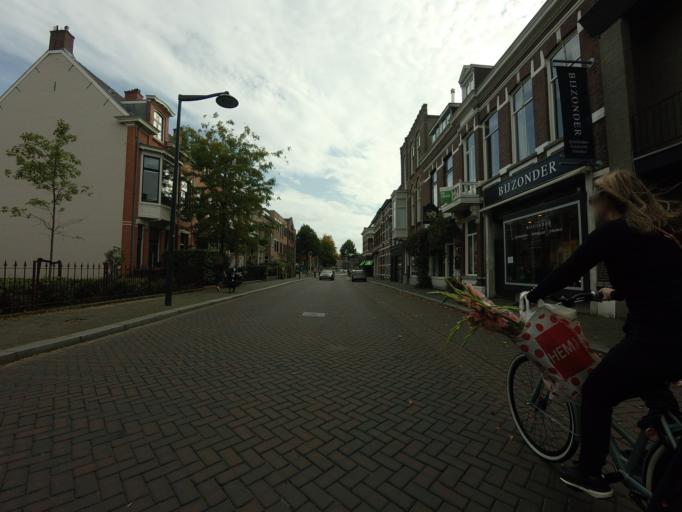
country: NL
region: North Brabant
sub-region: Gemeente Breda
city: Breda
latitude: 51.5745
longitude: 4.7828
